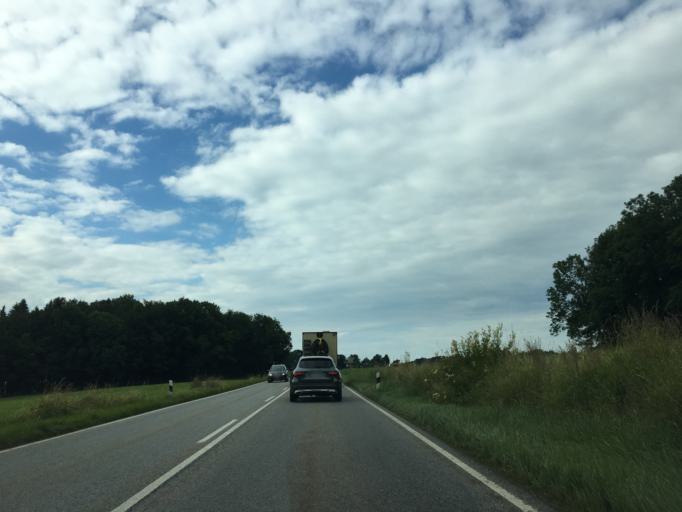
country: DE
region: Bavaria
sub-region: Upper Bavaria
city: Warngau
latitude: 47.8056
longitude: 11.7199
